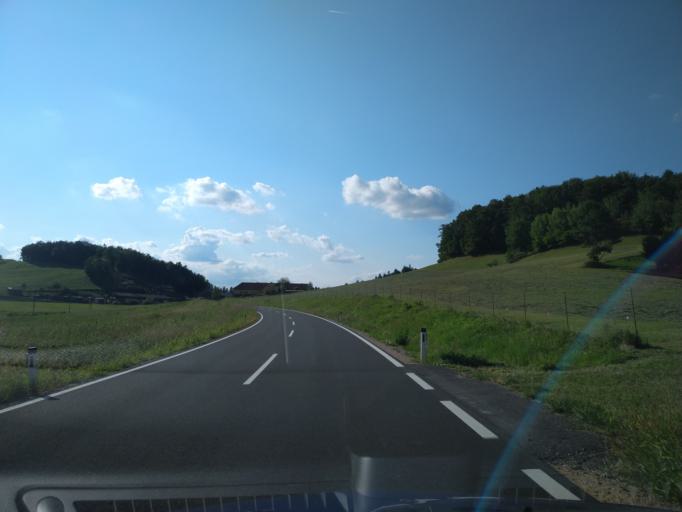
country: AT
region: Styria
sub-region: Politischer Bezirk Leibnitz
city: Gleinstatten
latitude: 46.7381
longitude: 15.3747
